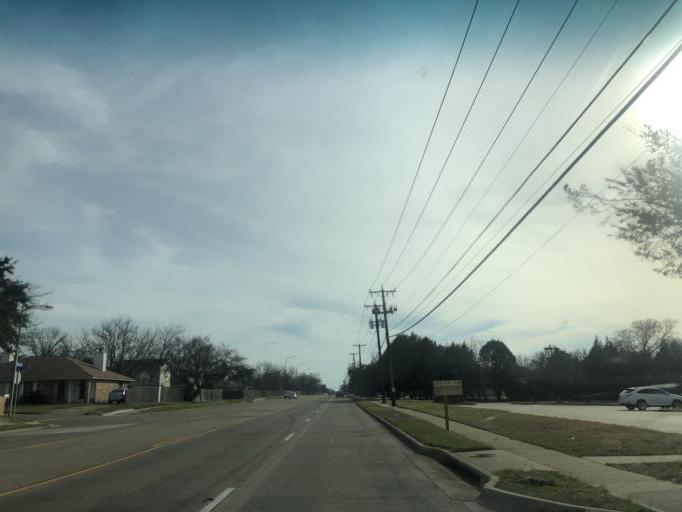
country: US
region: Texas
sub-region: Tarrant County
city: Dalworthington Gardens
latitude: 32.7050
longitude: -97.1493
